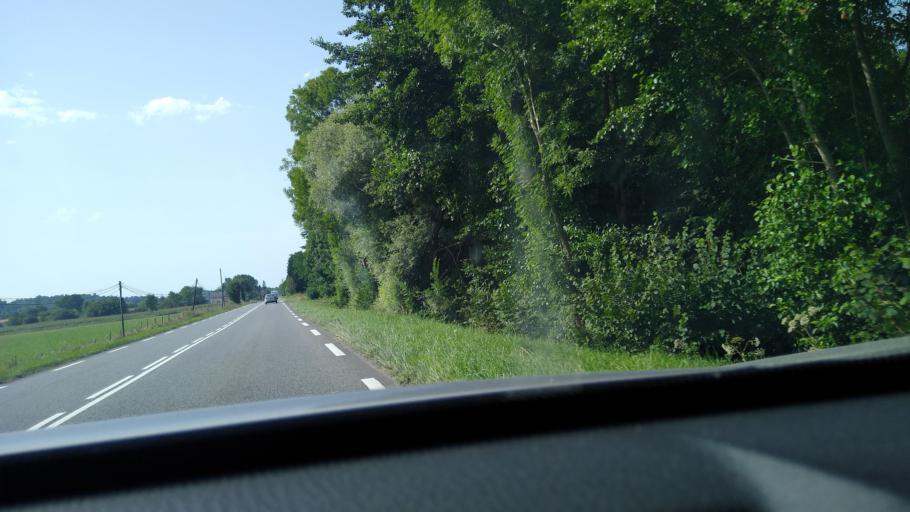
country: FR
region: Midi-Pyrenees
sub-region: Departement de la Haute-Garonne
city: Salies-du-Salat
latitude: 43.0483
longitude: 0.9857
